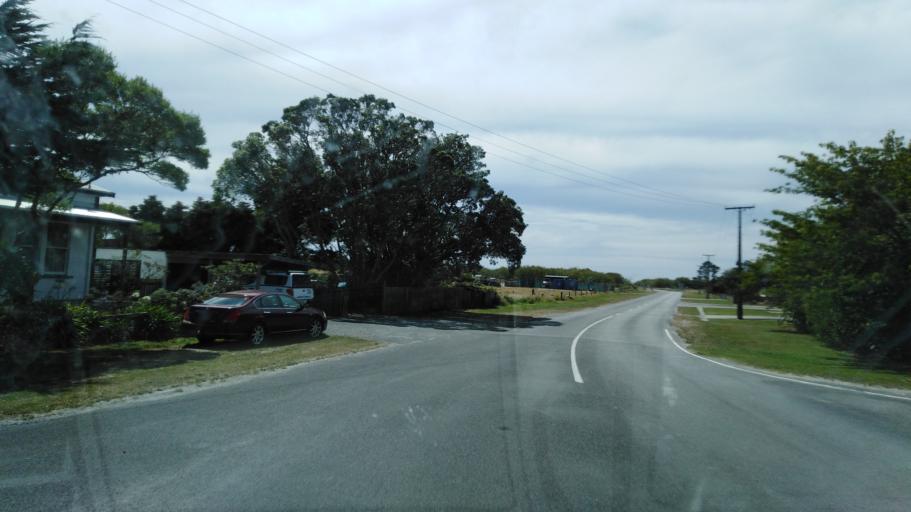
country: NZ
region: West Coast
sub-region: Buller District
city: Westport
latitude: -41.7406
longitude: 171.6028
